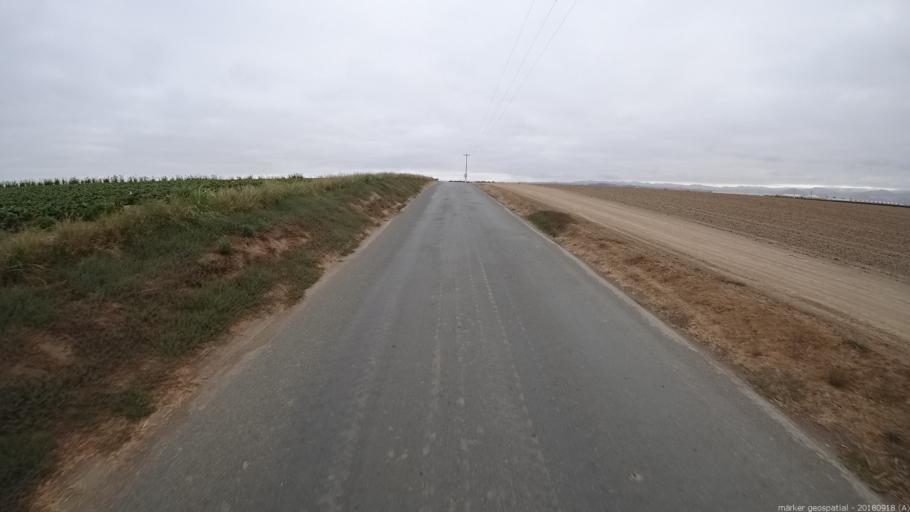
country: US
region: California
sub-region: Monterey County
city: Boronda
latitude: 36.7348
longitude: -121.6956
